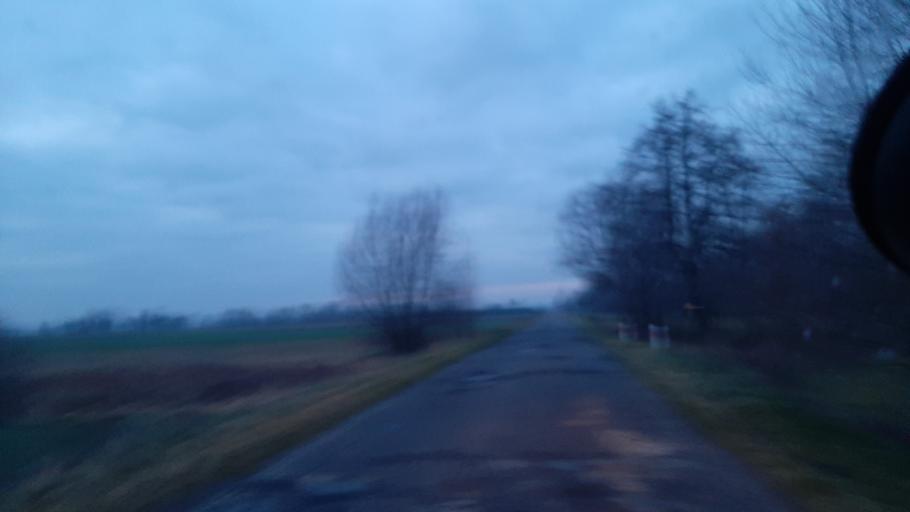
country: PL
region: Lublin Voivodeship
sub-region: Powiat lubartowski
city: Firlej
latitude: 51.6034
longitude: 22.5054
